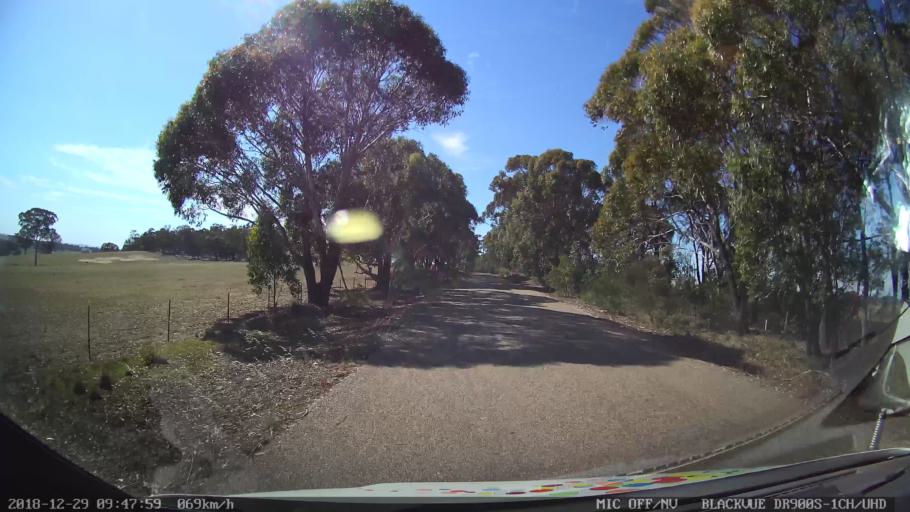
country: AU
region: New South Wales
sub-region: Upper Lachlan Shire
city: Crookwell
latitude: -34.7118
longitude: 149.4532
